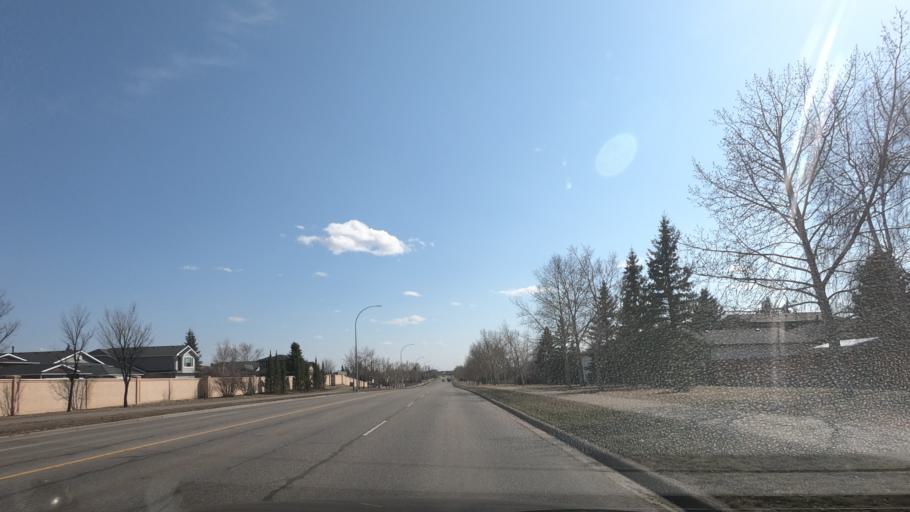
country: CA
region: Alberta
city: Airdrie
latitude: 51.2792
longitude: -113.9899
